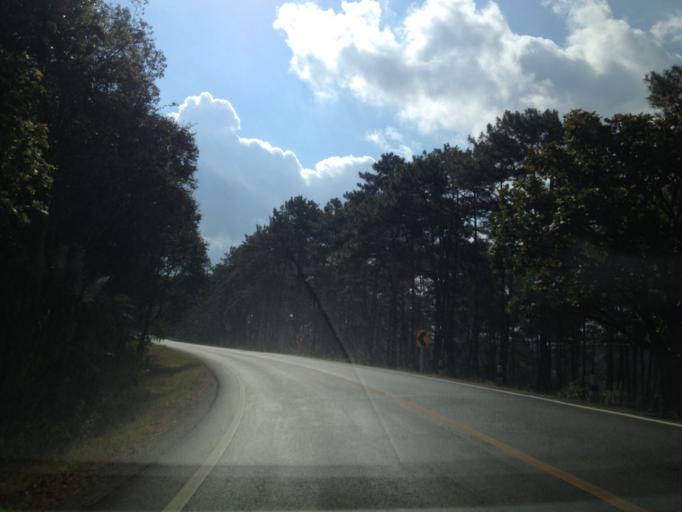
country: TH
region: Chiang Mai
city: Hot
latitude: 18.1415
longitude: 98.3249
